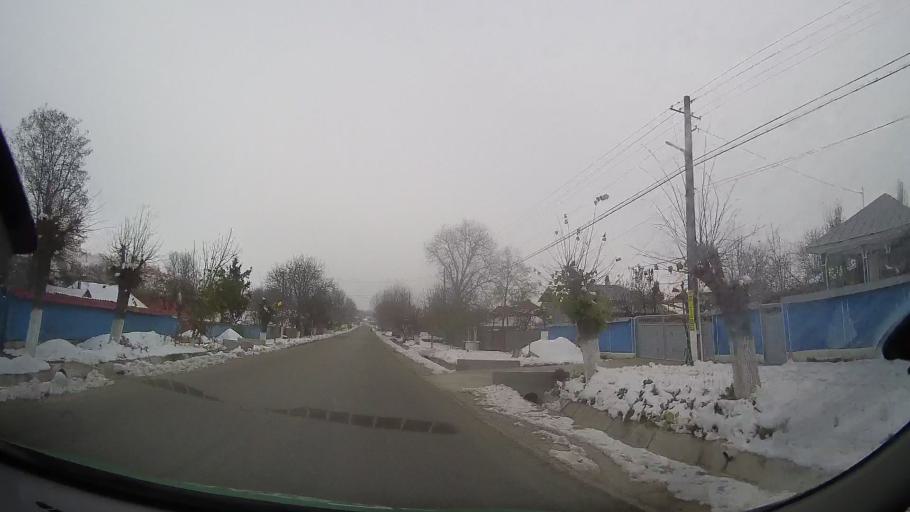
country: RO
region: Bacau
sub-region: Comuna Glavanesti
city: Frumuselu
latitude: 46.2961
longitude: 27.3004
